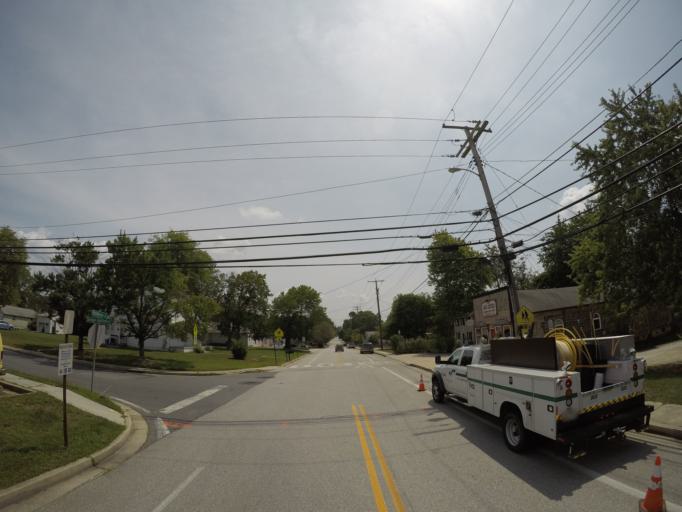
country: US
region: Maryland
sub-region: Howard County
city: Savage
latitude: 39.1379
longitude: -76.8243
